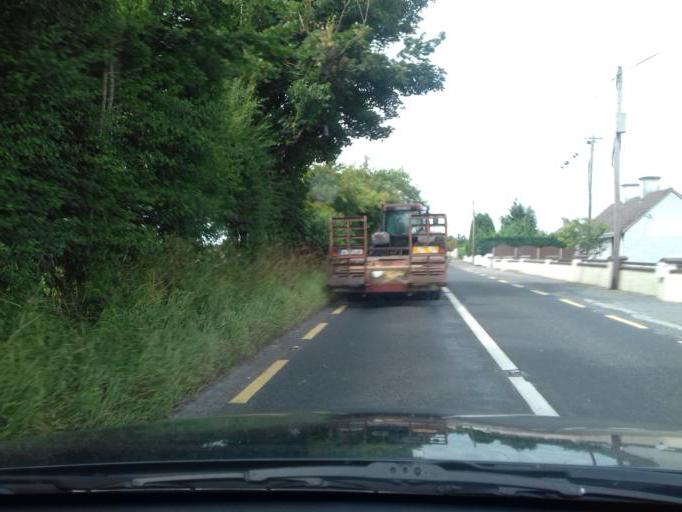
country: IE
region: Leinster
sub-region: County Carlow
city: Tullow
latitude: 52.8351
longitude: -6.7187
